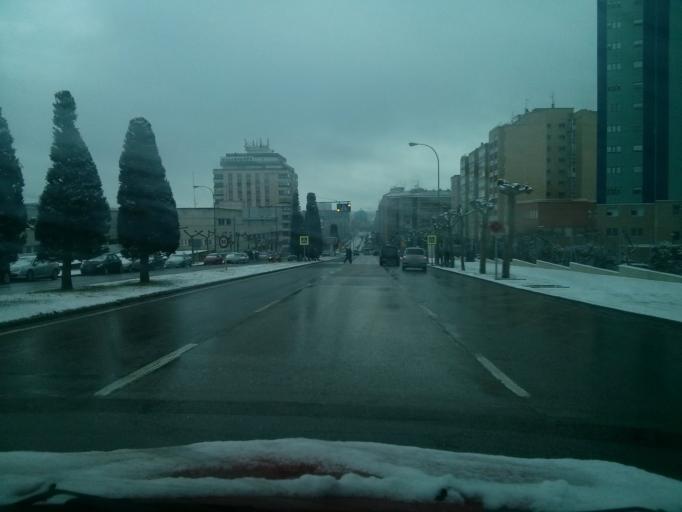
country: ES
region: Castille and Leon
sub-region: Provincia de Burgos
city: Burgos
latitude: 42.3568
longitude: -3.6929
